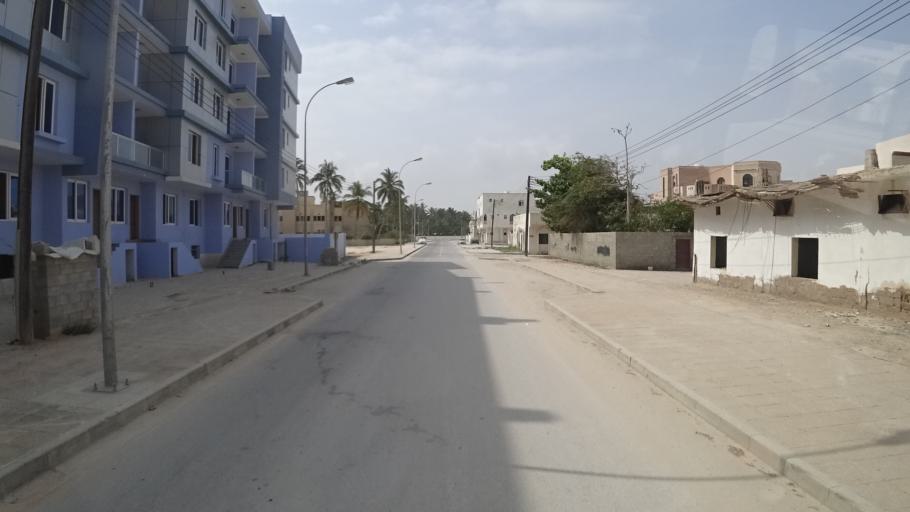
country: OM
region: Zufar
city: Salalah
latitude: 17.0096
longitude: 54.1574
